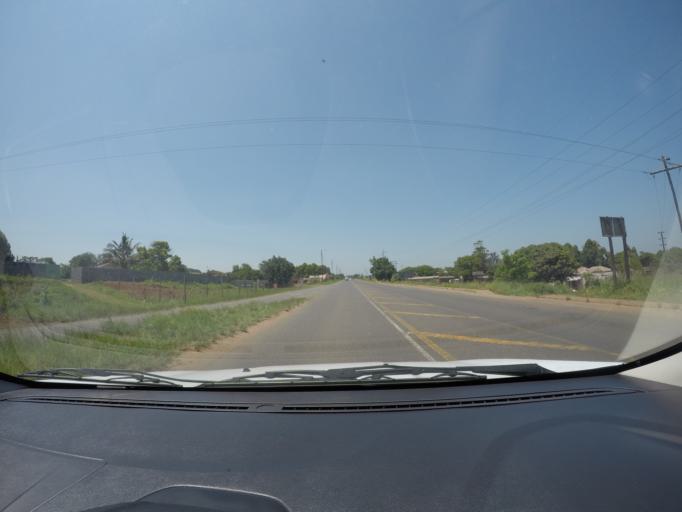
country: ZA
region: KwaZulu-Natal
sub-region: uThungulu District Municipality
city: eSikhawini
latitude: -28.8407
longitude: 31.9352
